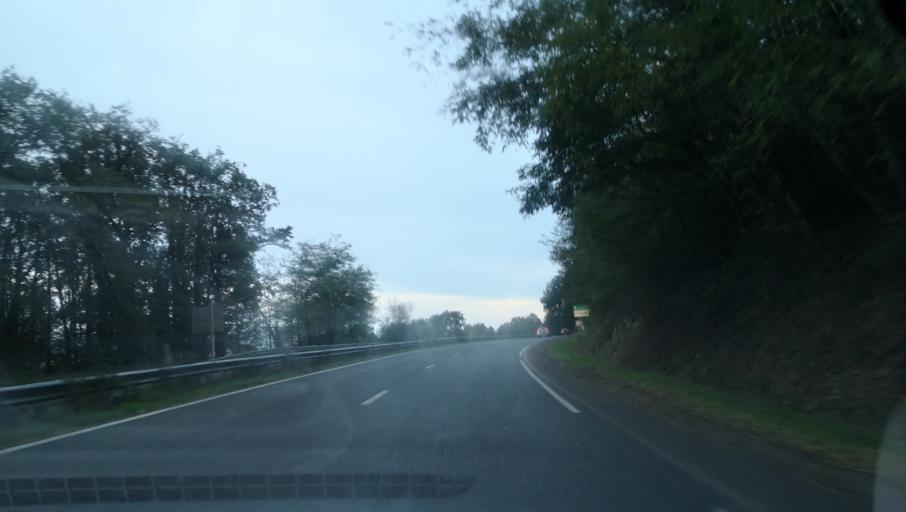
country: FR
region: Midi-Pyrenees
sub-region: Departement du Lot
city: Pradines
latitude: 44.5080
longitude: 1.4458
